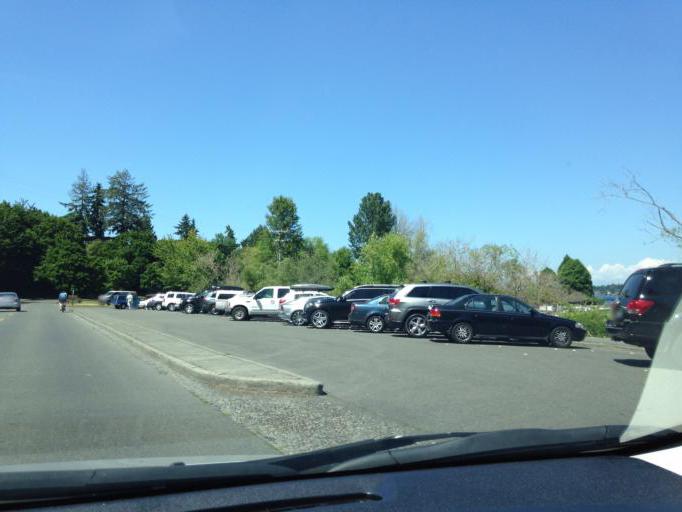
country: US
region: Washington
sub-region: King County
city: Mercer Island
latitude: 47.5627
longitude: -122.2681
